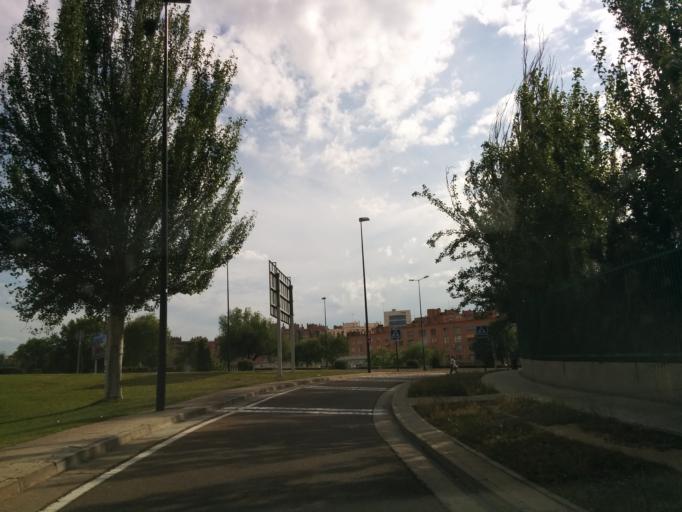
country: ES
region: Aragon
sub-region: Provincia de Zaragoza
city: Zaragoza
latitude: 41.6736
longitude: -0.8814
